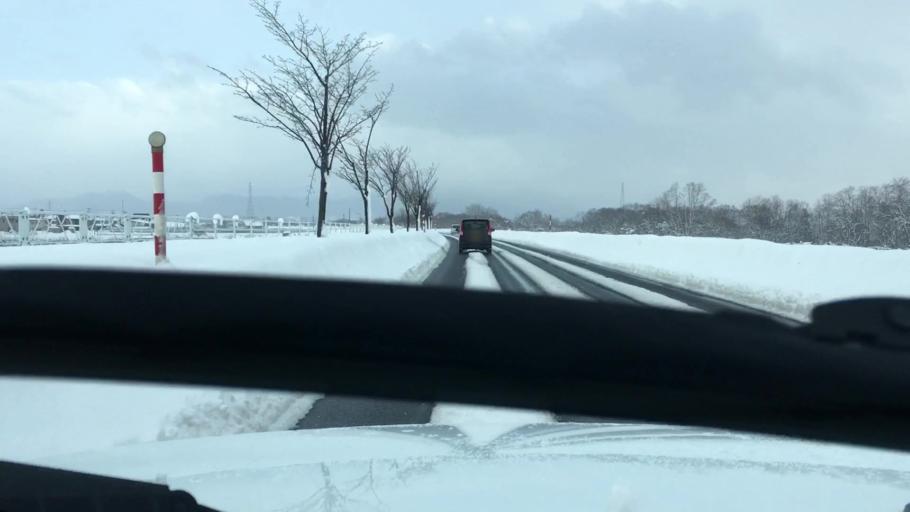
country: JP
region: Aomori
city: Hirosaki
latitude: 40.6380
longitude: 140.4717
